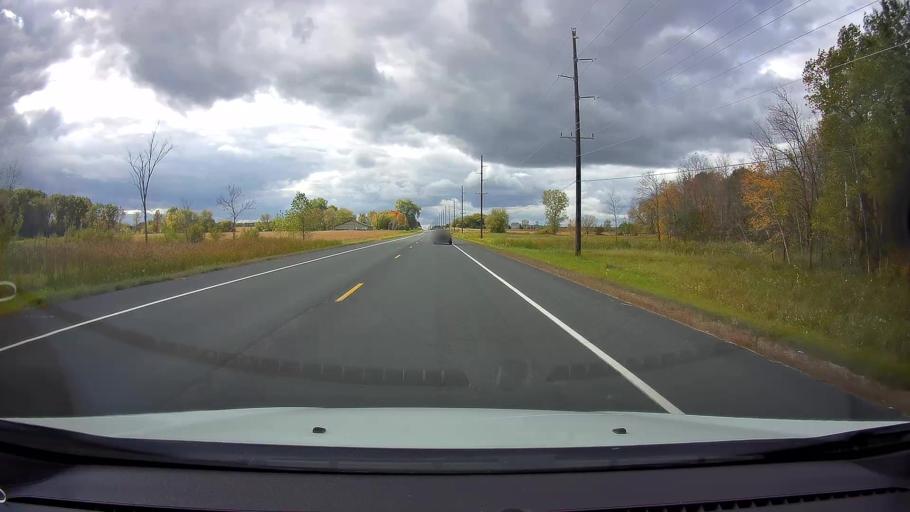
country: US
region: Minnesota
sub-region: Chisago County
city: Shafer
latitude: 45.3973
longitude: -92.7359
